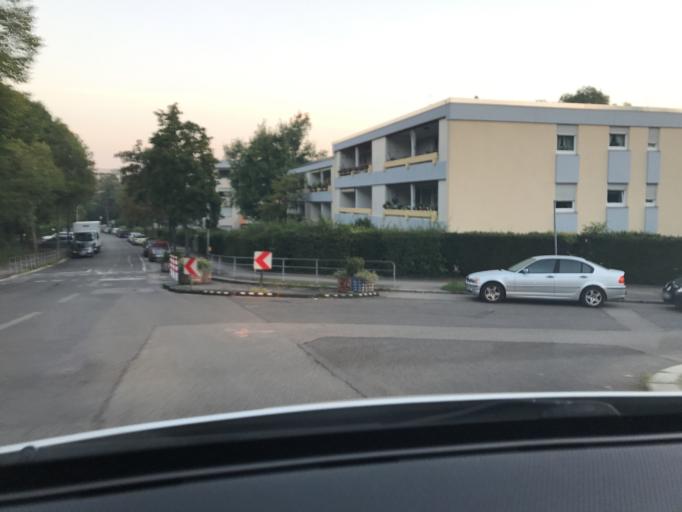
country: DE
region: Baden-Wuerttemberg
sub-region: Regierungsbezirk Stuttgart
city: Sindelfingen
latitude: 48.7012
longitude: 9.0207
